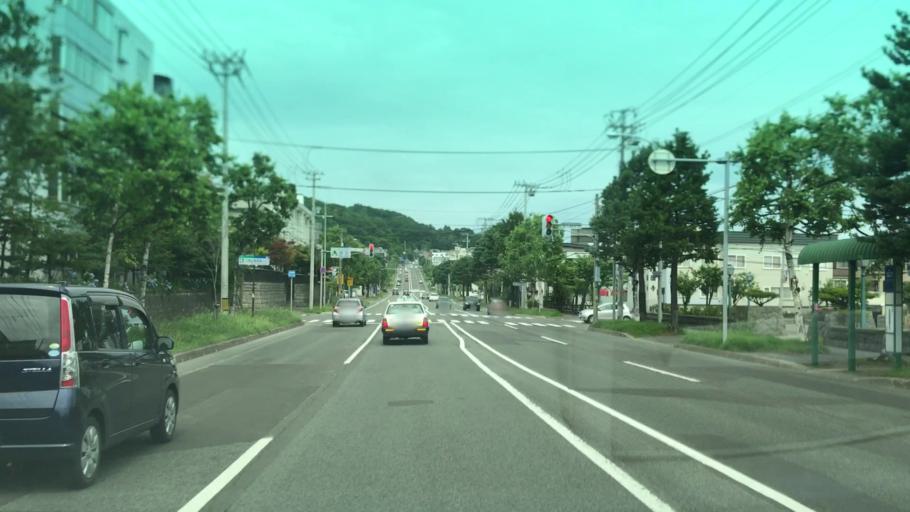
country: JP
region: Hokkaido
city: Sapporo
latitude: 43.0606
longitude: 141.2969
